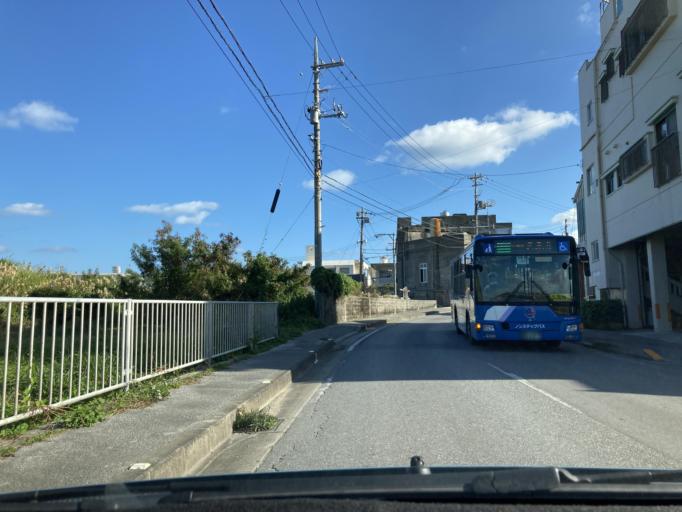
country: JP
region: Okinawa
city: Katsuren-haebaru
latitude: 26.3107
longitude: 127.9117
